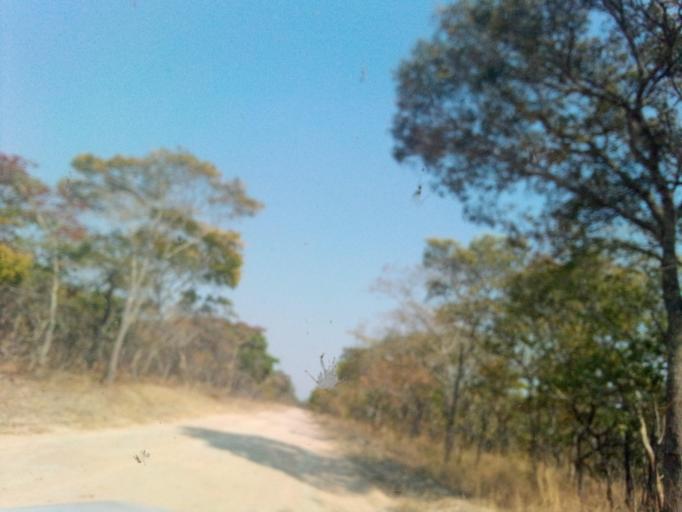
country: ZM
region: Northern
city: Mpika
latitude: -12.2266
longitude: 30.9042
